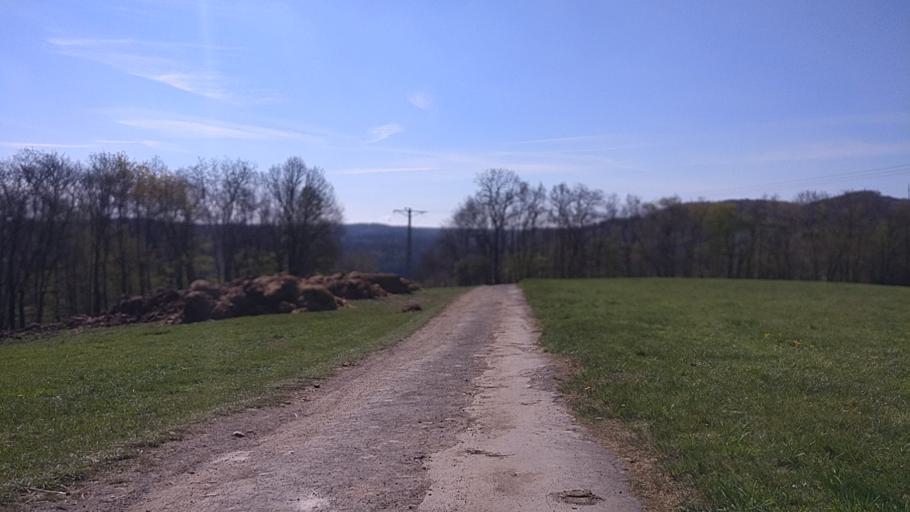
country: DE
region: Rheinland-Pfalz
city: Peterslahr
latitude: 50.6303
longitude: 7.4385
